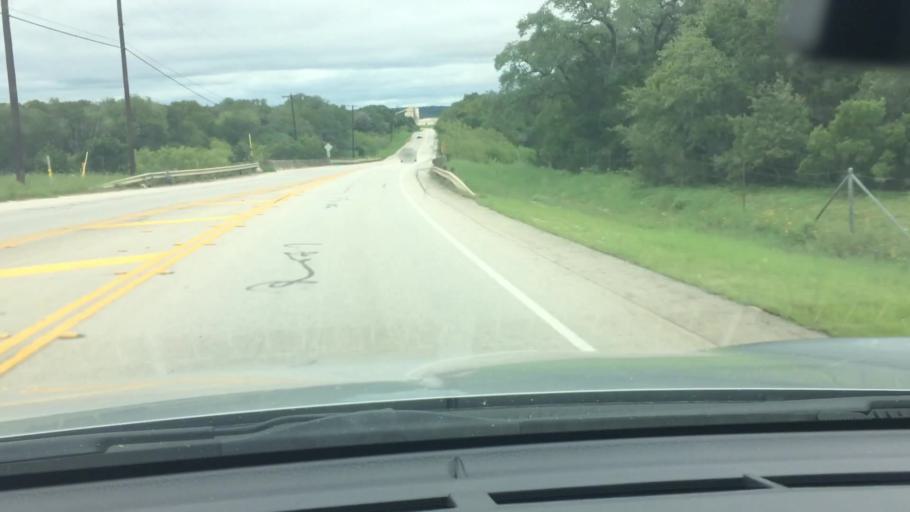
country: US
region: Texas
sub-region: Bexar County
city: Live Oak
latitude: 29.6111
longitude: -98.3667
